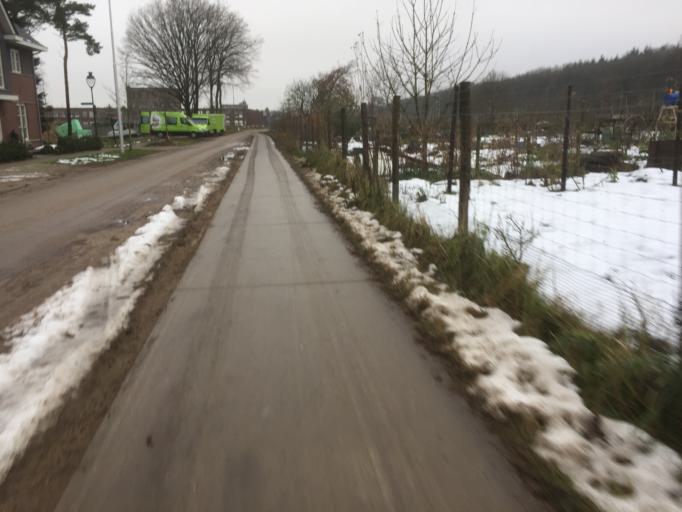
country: NL
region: Gelderland
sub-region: Gemeente Ede
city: Bennekom
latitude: 52.0246
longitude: 5.6851
